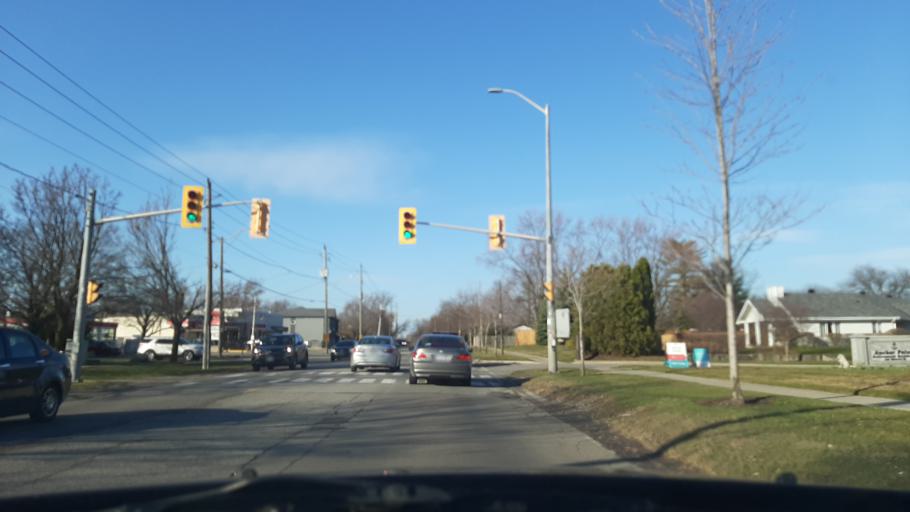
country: CA
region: Ontario
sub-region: Regional Municipality of Niagara
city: St. Catharines
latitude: 43.1899
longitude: -79.2624
